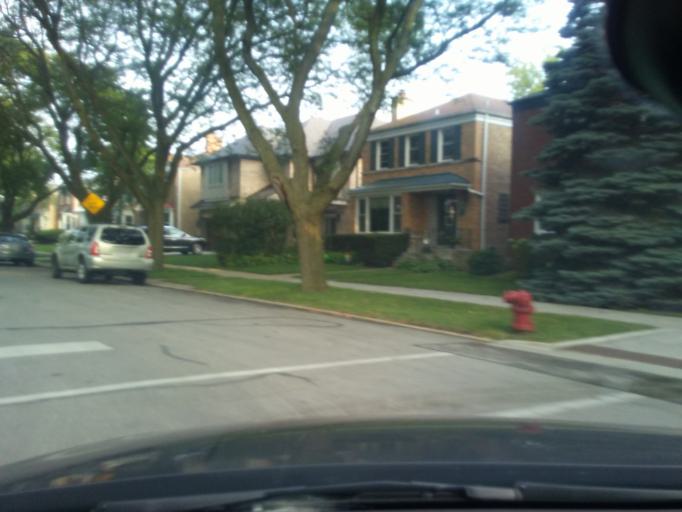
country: US
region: Illinois
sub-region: Cook County
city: Evanston
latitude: 42.0165
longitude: -87.7021
